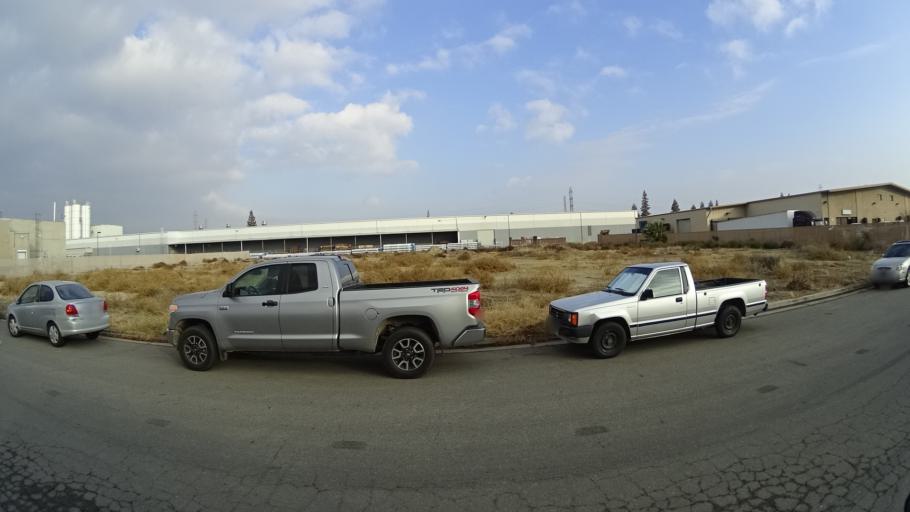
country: US
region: California
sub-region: Kern County
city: Greenacres
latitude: 35.3144
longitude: -119.0773
